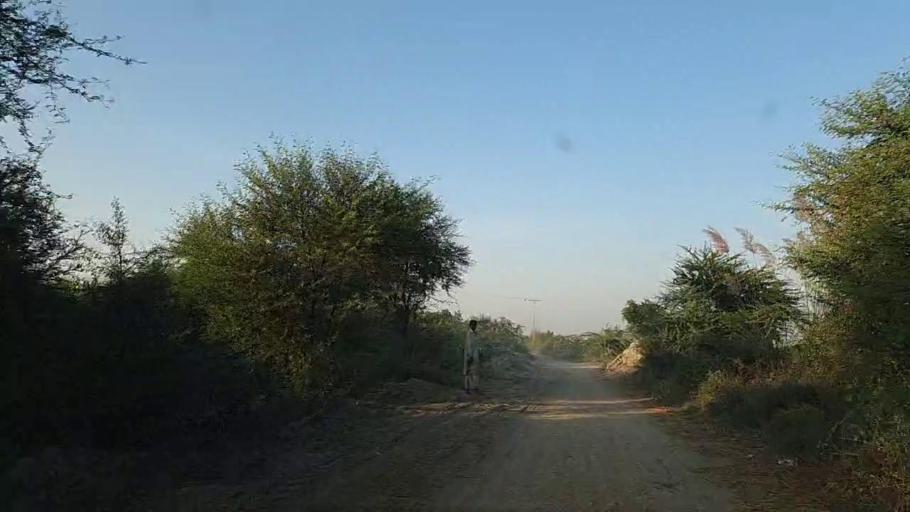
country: PK
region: Sindh
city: Mirpur Batoro
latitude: 24.7208
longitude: 68.2139
